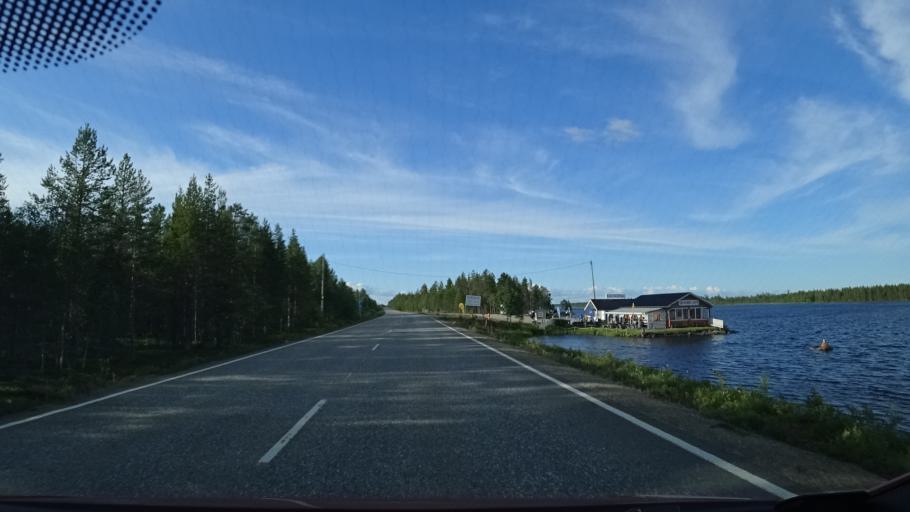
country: FI
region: Lapland
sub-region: Pohjois-Lappi
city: Sodankylae
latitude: 67.7391
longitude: 26.7600
